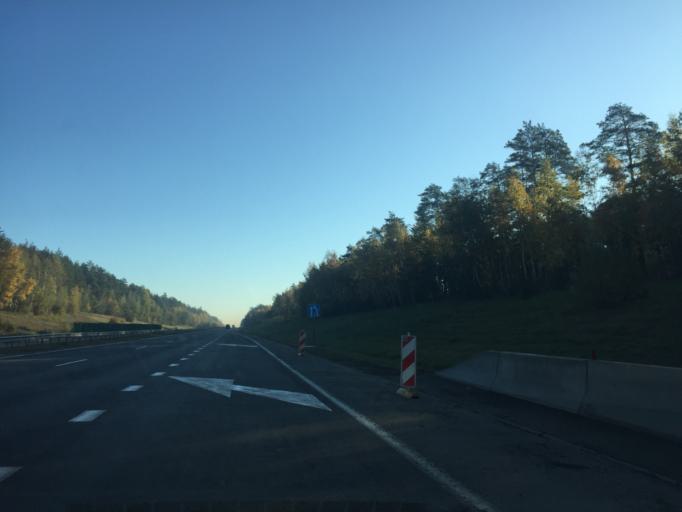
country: BY
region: Minsk
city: Pryvol'ny
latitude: 53.7941
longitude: 27.7420
